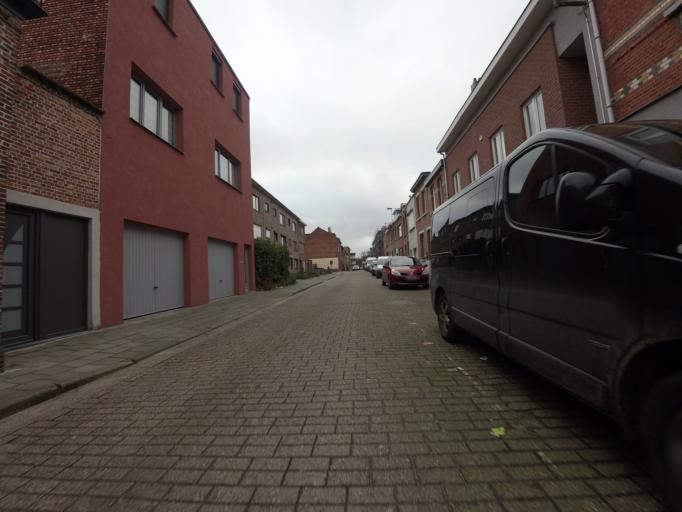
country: BE
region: Flanders
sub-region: Provincie Antwerpen
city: Hoboken
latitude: 51.1739
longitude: 4.3591
